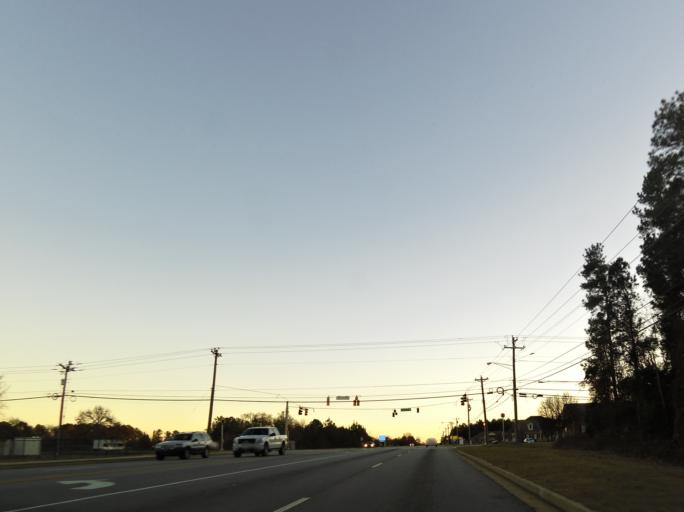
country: US
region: Georgia
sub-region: Houston County
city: Centerville
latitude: 32.6026
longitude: -83.6652
